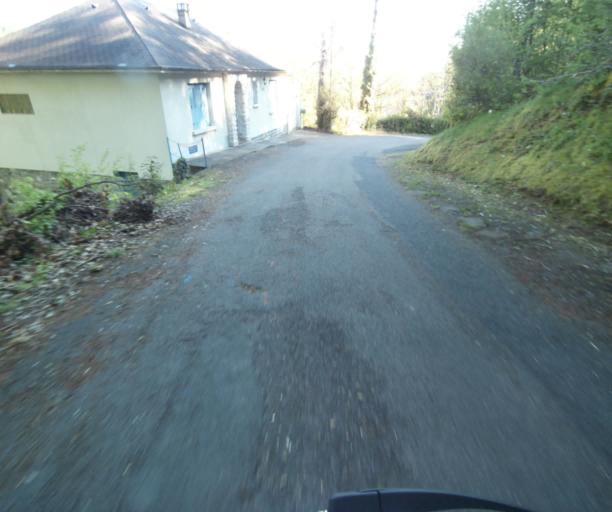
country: FR
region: Limousin
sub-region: Departement de la Correze
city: Tulle
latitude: 45.2598
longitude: 1.7649
